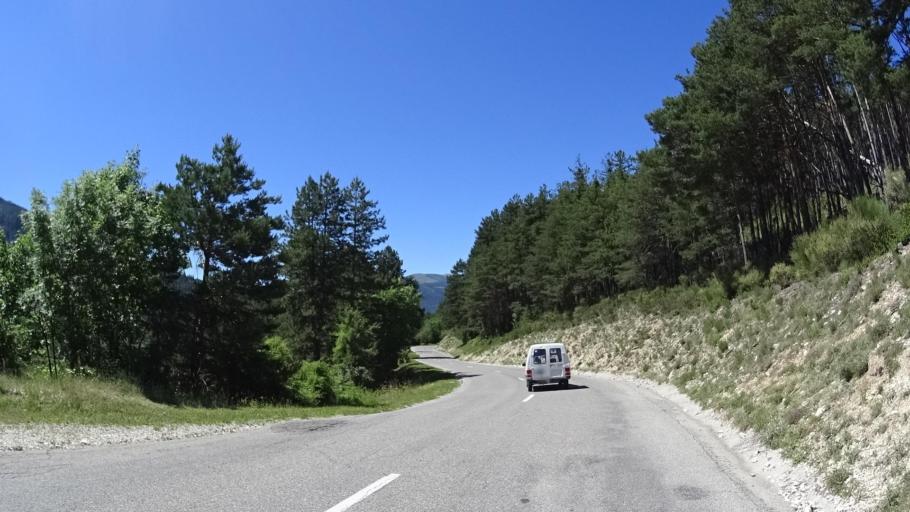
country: FR
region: Provence-Alpes-Cote d'Azur
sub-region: Departement des Alpes-de-Haute-Provence
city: Annot
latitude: 43.9902
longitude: 6.5354
